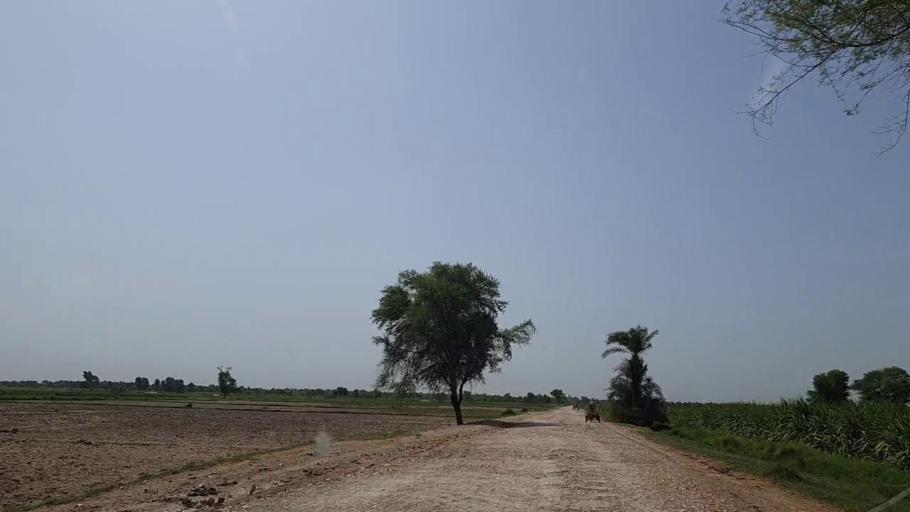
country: PK
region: Sindh
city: Naushahro Firoz
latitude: 26.8417
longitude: 68.0149
